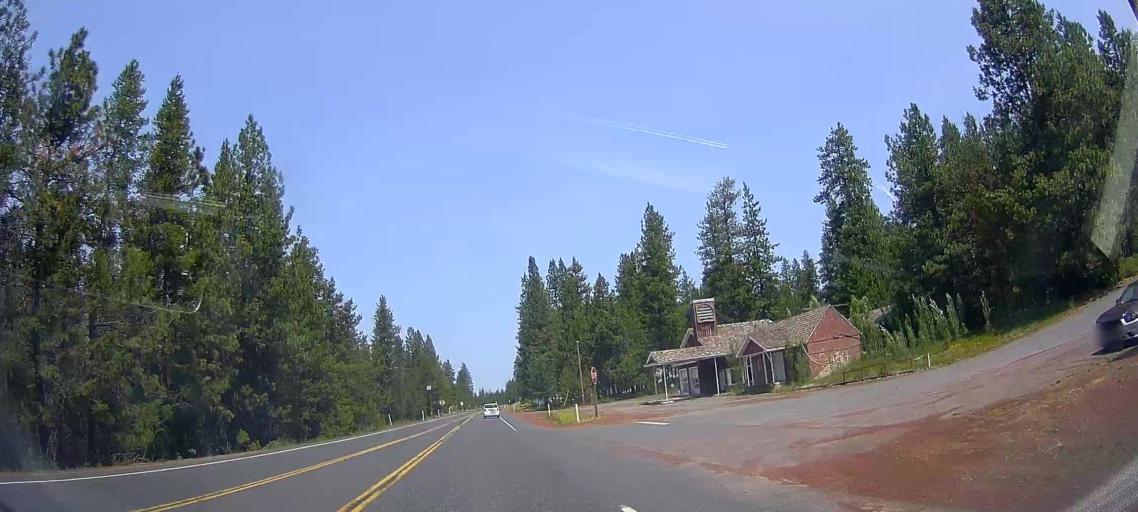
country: US
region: Oregon
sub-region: Deschutes County
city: La Pine
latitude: 43.4788
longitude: -121.6873
